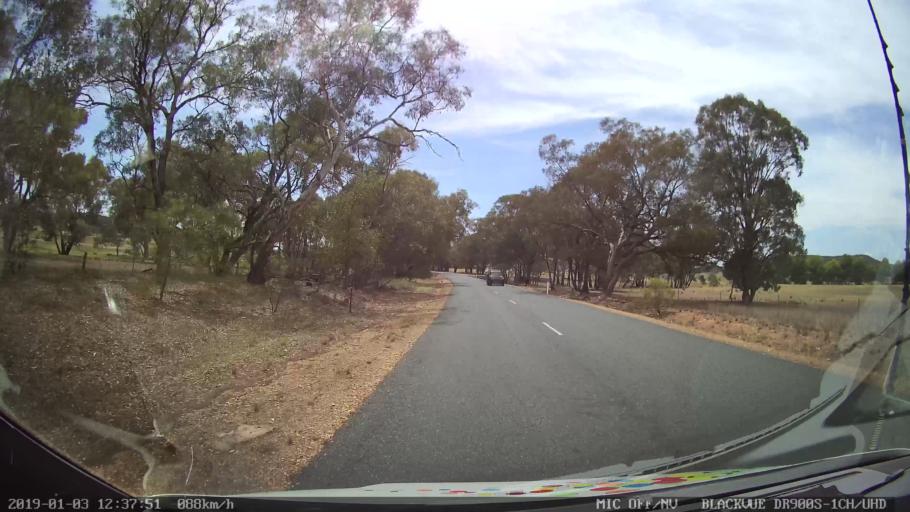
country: AU
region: New South Wales
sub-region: Weddin
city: Grenfell
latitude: -33.8390
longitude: 148.1890
